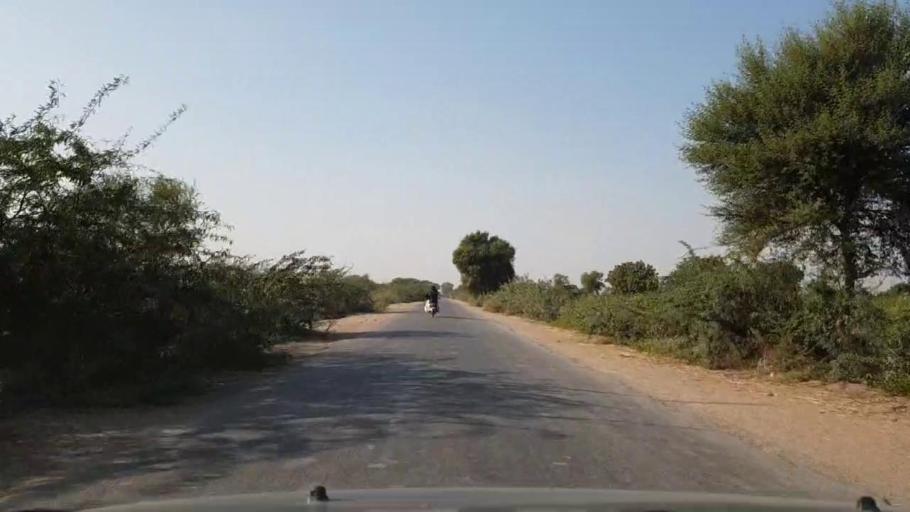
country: PK
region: Sindh
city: Tando Ghulam Ali
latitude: 25.1462
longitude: 68.8654
